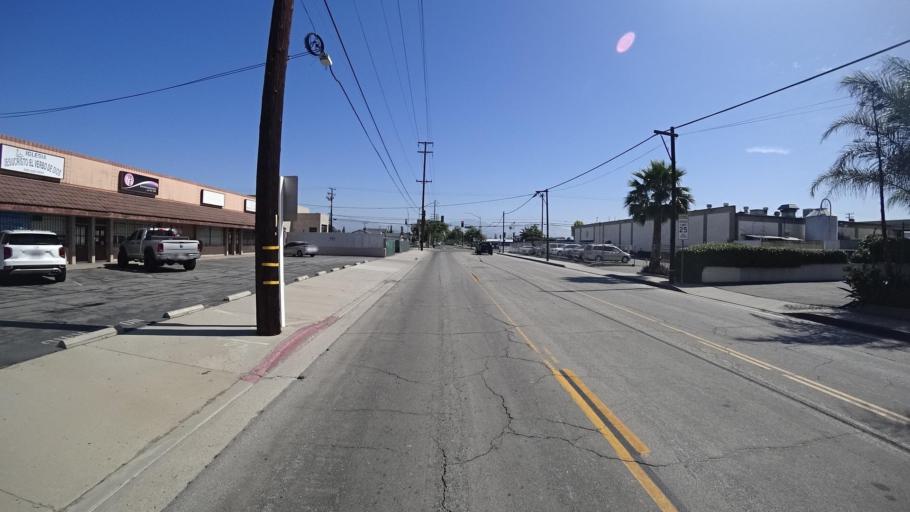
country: US
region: California
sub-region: Los Angeles County
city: West Puente Valley
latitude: 34.0329
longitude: -117.9679
